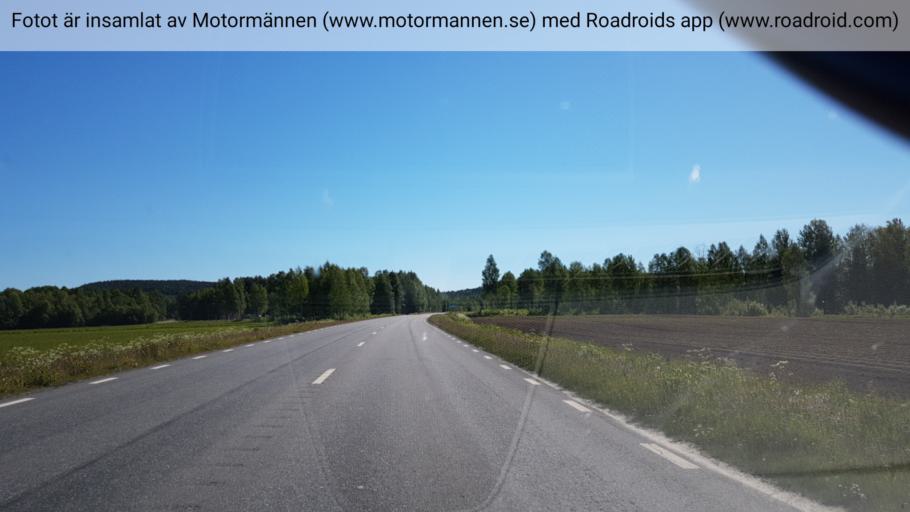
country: SE
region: Norrbotten
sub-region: Bodens Kommun
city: Boden
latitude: 65.8512
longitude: 21.5651
